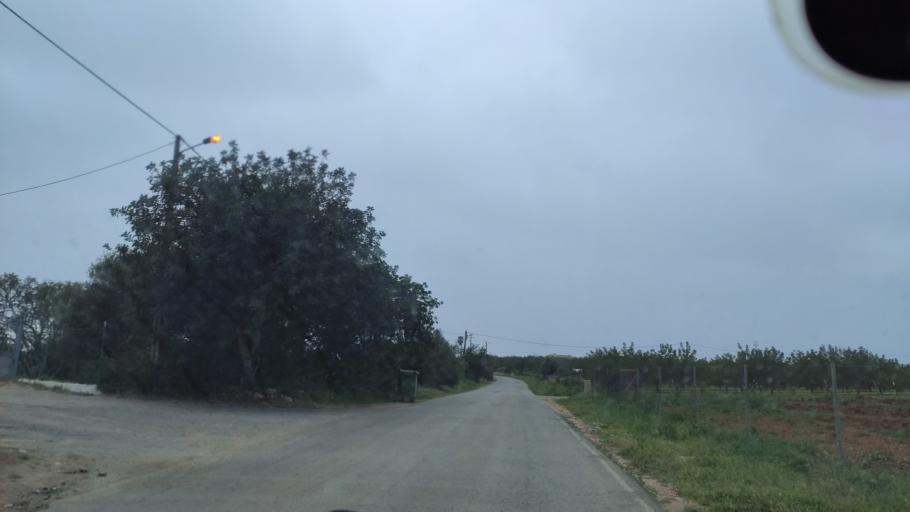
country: PT
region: Faro
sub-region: Faro
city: Santa Barbara de Nexe
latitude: 37.0805
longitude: -7.9272
